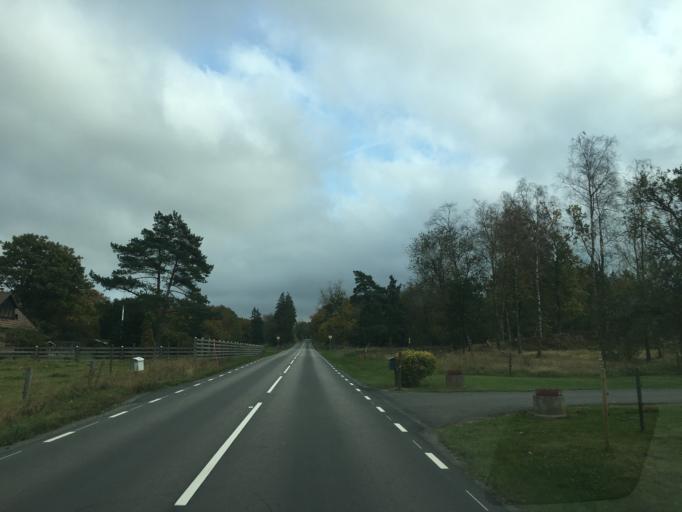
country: SE
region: Skane
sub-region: Tomelilla Kommun
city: Tomelilla
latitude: 55.6370
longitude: 14.0780
